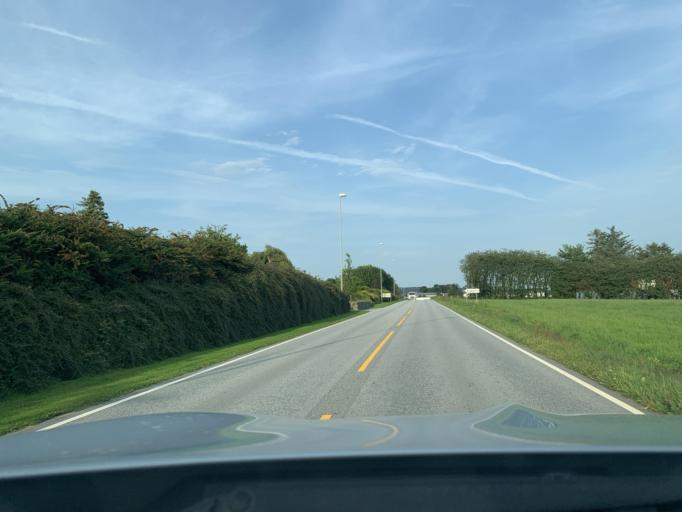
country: NO
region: Rogaland
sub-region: Time
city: Bryne
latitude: 58.7394
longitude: 5.6149
